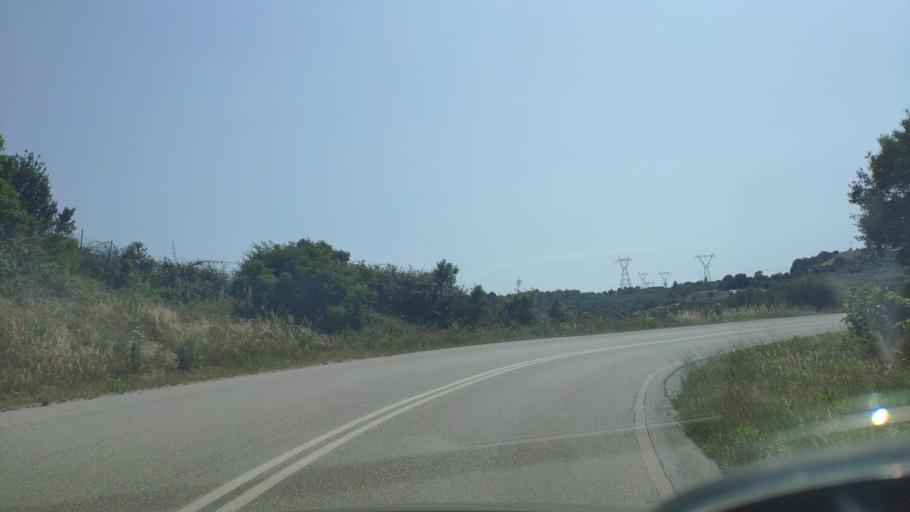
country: GR
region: Epirus
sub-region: Nomos Artas
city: Ano Kalentini
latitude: 39.2130
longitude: 21.1234
